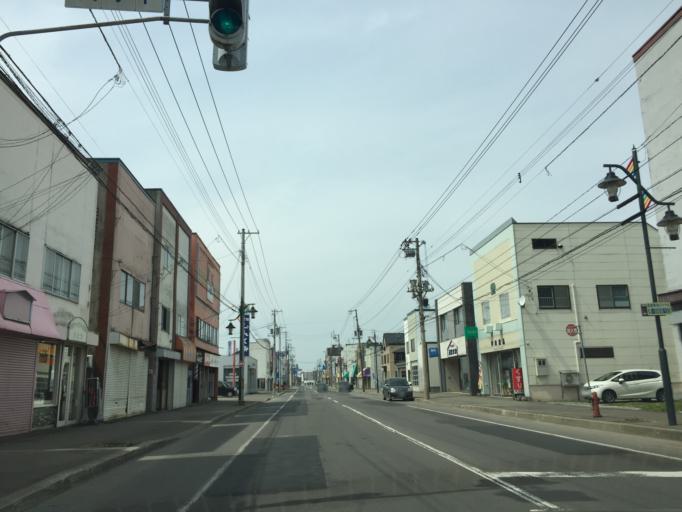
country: JP
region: Hokkaido
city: Akabira
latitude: 43.5540
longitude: 142.0521
